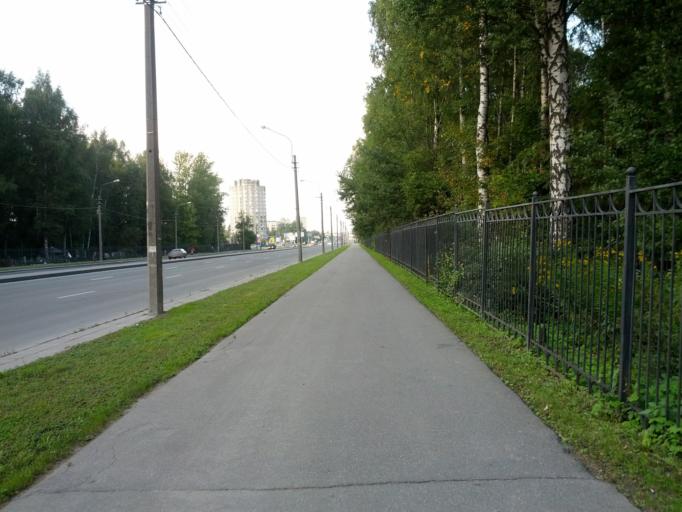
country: RU
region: St.-Petersburg
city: Krasnogvargeisky
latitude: 59.9491
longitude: 30.4367
